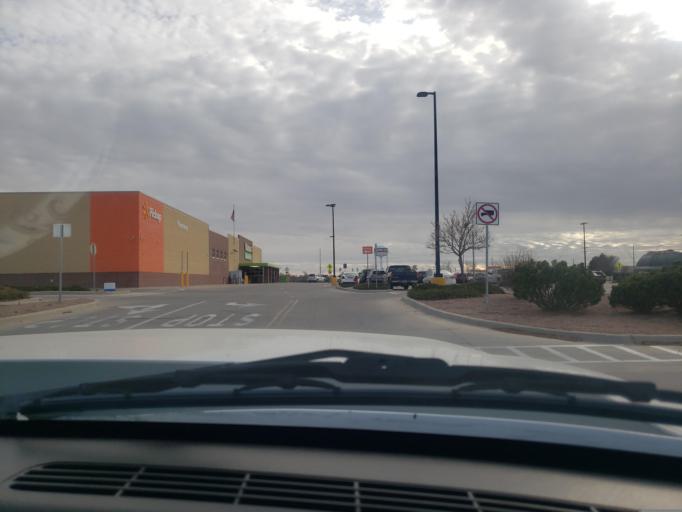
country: US
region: Kansas
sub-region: Finney County
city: Garden City
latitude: 37.9876
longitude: -100.8820
